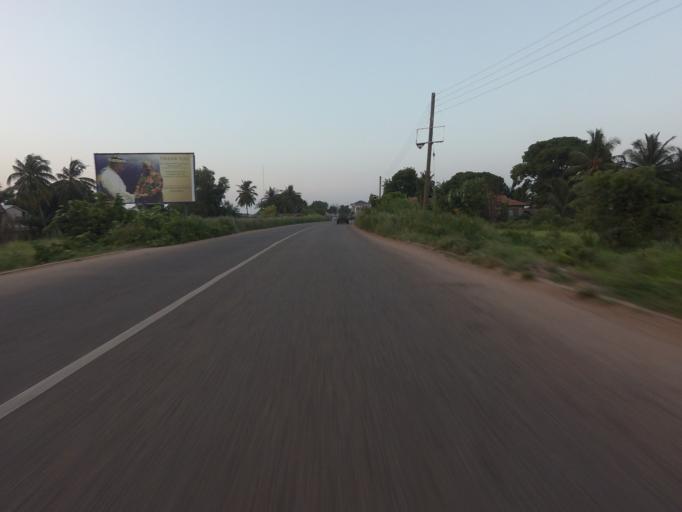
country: GH
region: Volta
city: Keta
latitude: 5.8763
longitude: 0.9807
